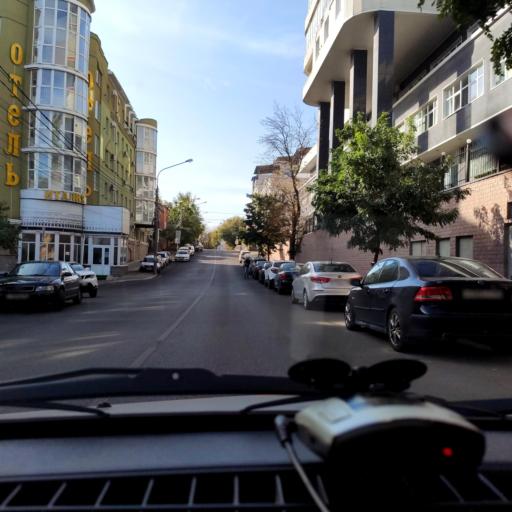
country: RU
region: Voronezj
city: Voronezh
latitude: 51.6780
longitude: 39.2185
